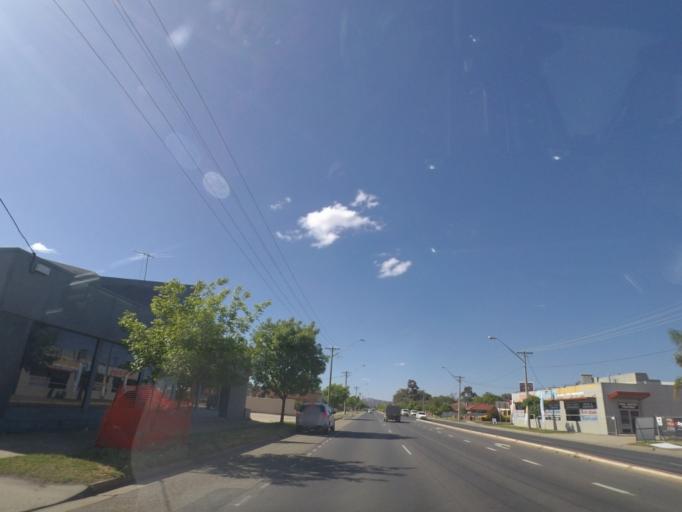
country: AU
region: New South Wales
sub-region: Albury Municipality
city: North Albury
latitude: -36.0669
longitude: 146.9308
